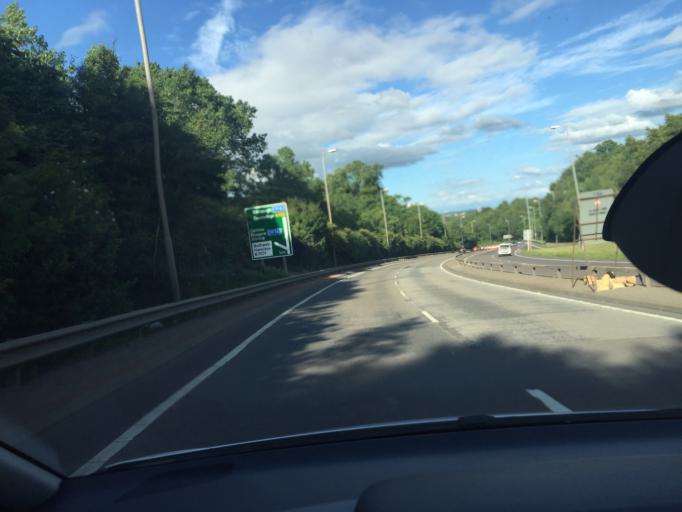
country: GB
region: Scotland
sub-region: South Lanarkshire
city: Bothwell
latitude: 55.7942
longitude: -4.0649
